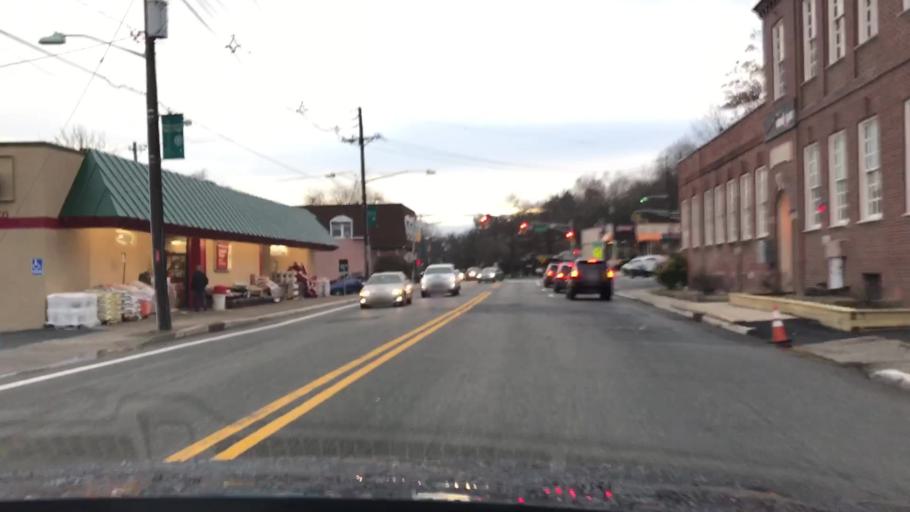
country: US
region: New Jersey
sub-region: Bergen County
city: New Milford
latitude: 40.9407
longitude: -74.0304
